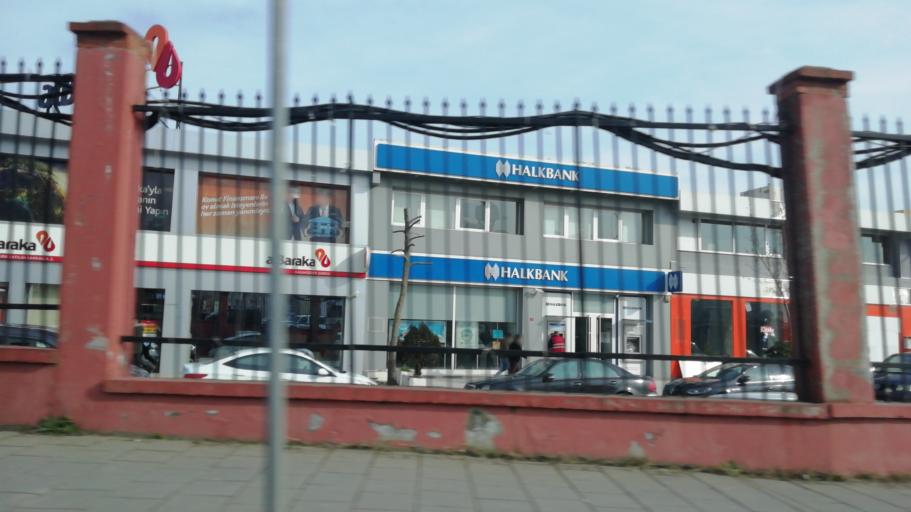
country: TR
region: Istanbul
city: Basaksehir
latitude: 41.0992
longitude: 28.7921
